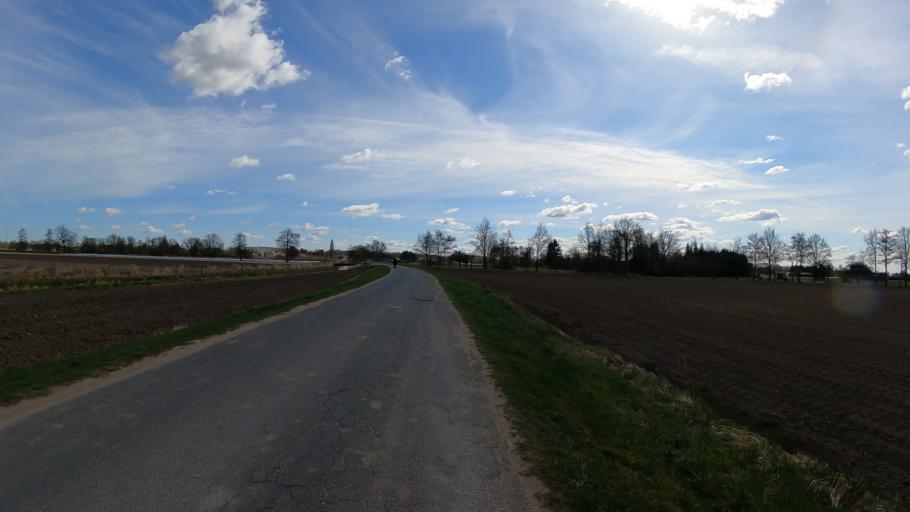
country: DE
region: Lower Saxony
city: Winsen
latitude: 53.4100
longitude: 10.1934
